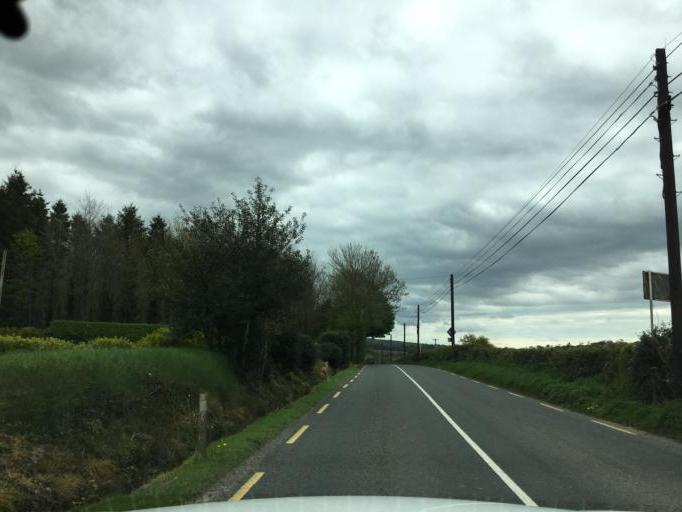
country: IE
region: Leinster
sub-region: Loch Garman
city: New Ross
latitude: 52.4271
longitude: -6.9460
